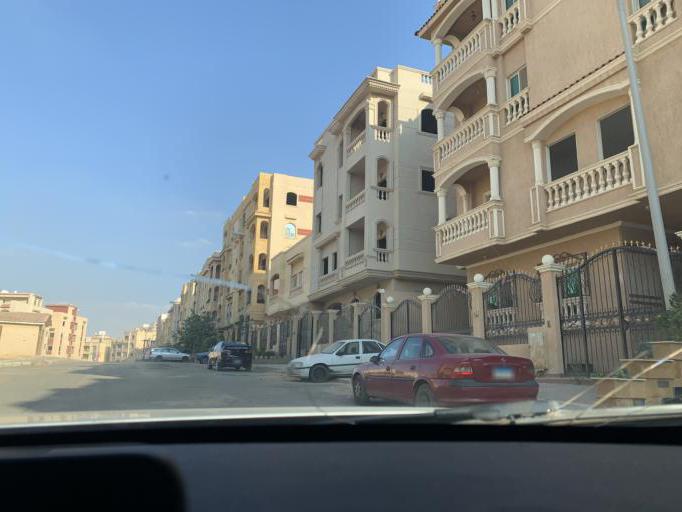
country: EG
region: Muhafazat al Qalyubiyah
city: Al Khankah
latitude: 30.0013
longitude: 31.4848
